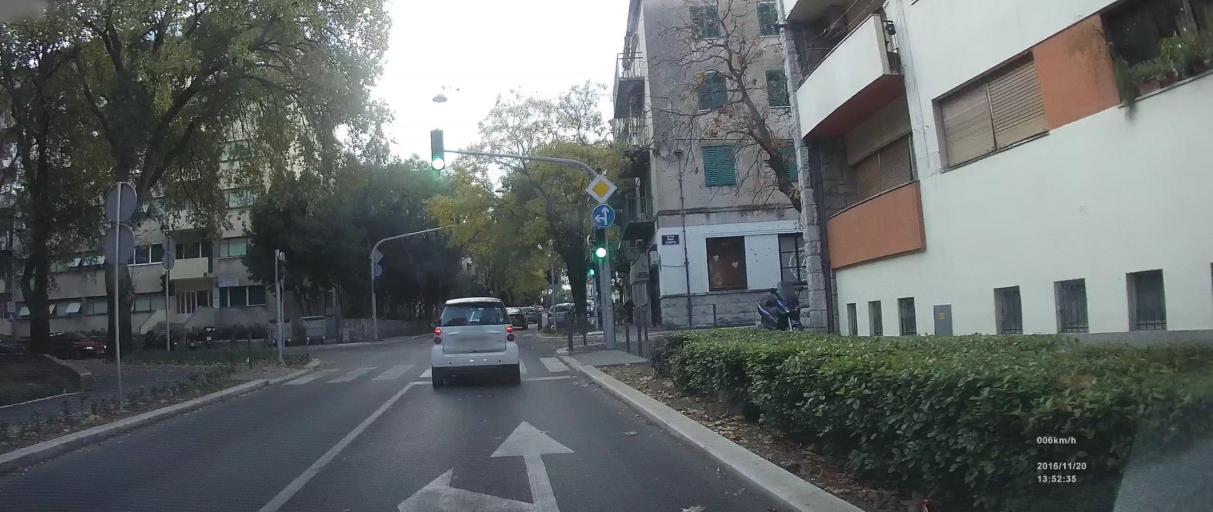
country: HR
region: Splitsko-Dalmatinska
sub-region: Grad Split
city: Split
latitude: 43.5130
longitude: 16.4328
